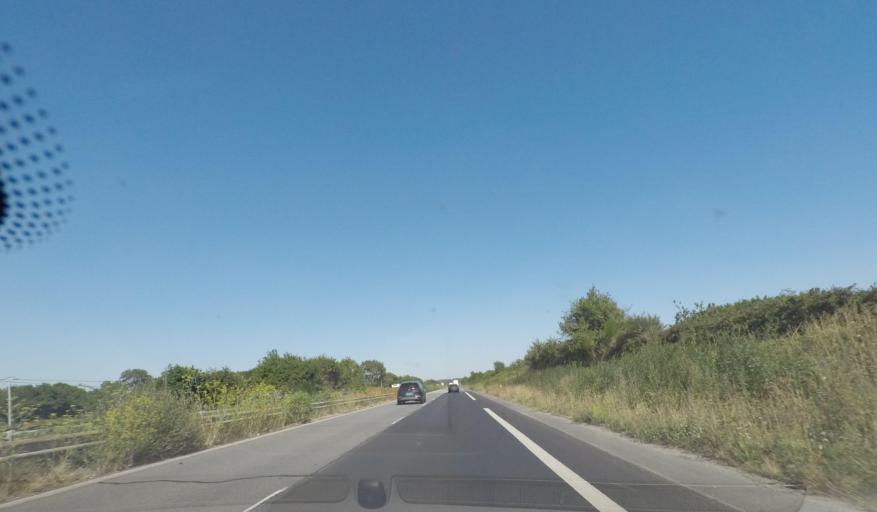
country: FR
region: Brittany
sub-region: Departement du Morbihan
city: Peaule
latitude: 47.5370
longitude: -2.3917
